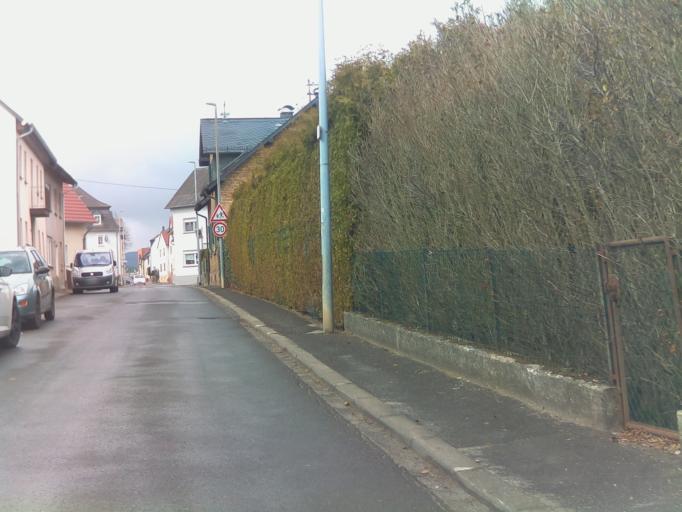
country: DE
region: Rheinland-Pfalz
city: Dorrebach
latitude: 49.9441
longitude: 7.7227
